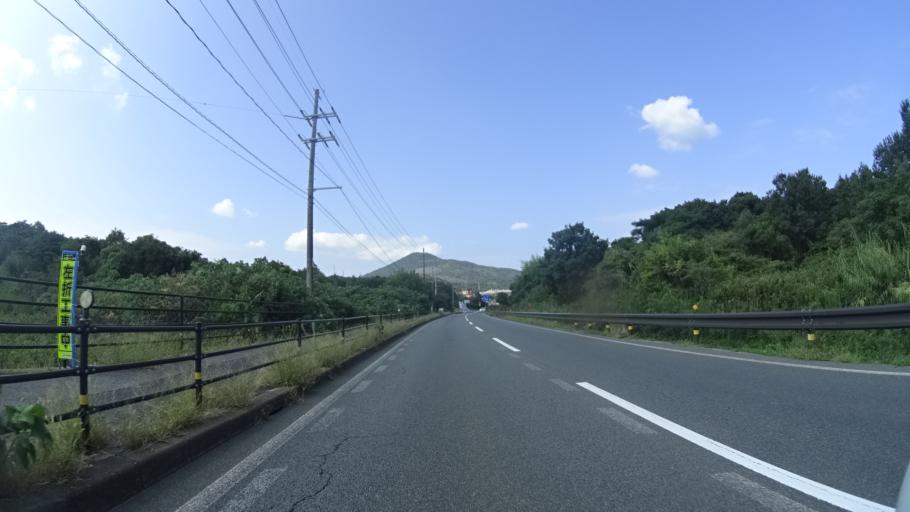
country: JP
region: Shimane
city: Gotsucho
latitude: 35.0379
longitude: 132.2831
